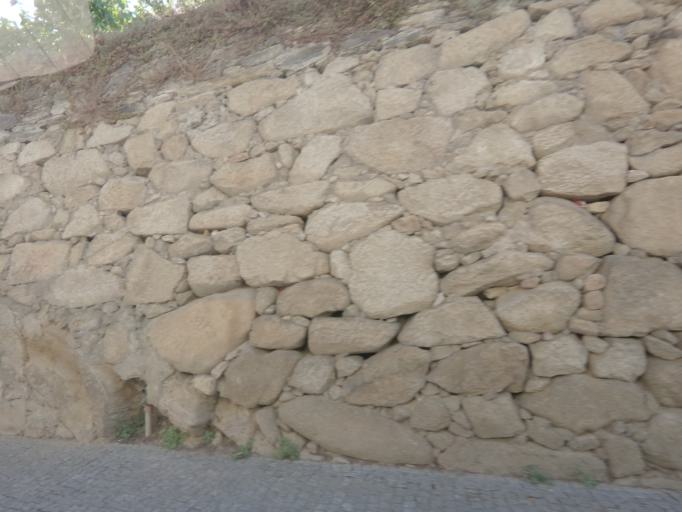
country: PT
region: Viseu
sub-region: Tabuaco
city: Tabuaco
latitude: 41.1164
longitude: -7.5669
